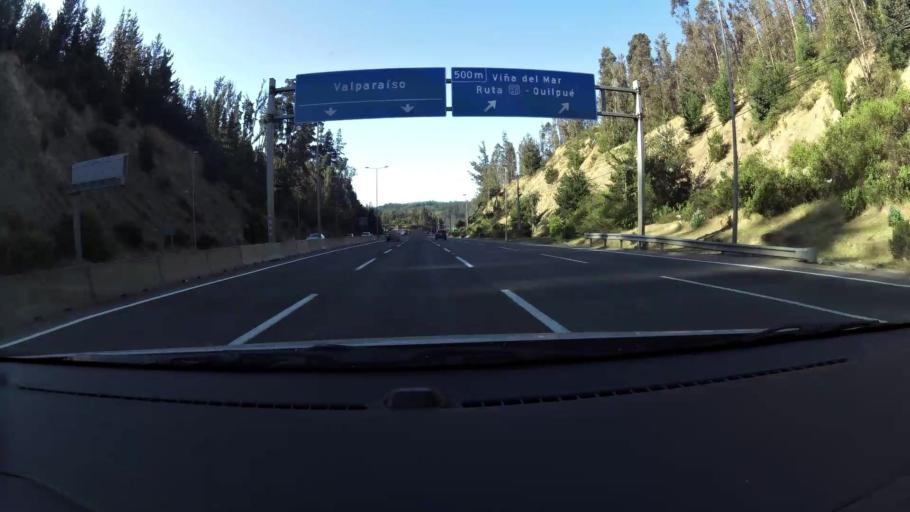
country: CL
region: Valparaiso
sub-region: Provincia de Valparaiso
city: Vina del Mar
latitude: -33.1036
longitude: -71.5482
